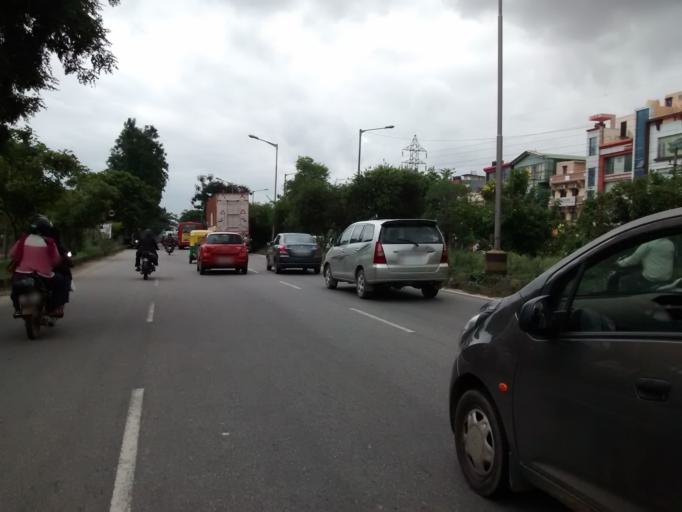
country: IN
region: Karnataka
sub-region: Bangalore Urban
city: Bangalore
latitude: 13.0204
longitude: 77.6519
